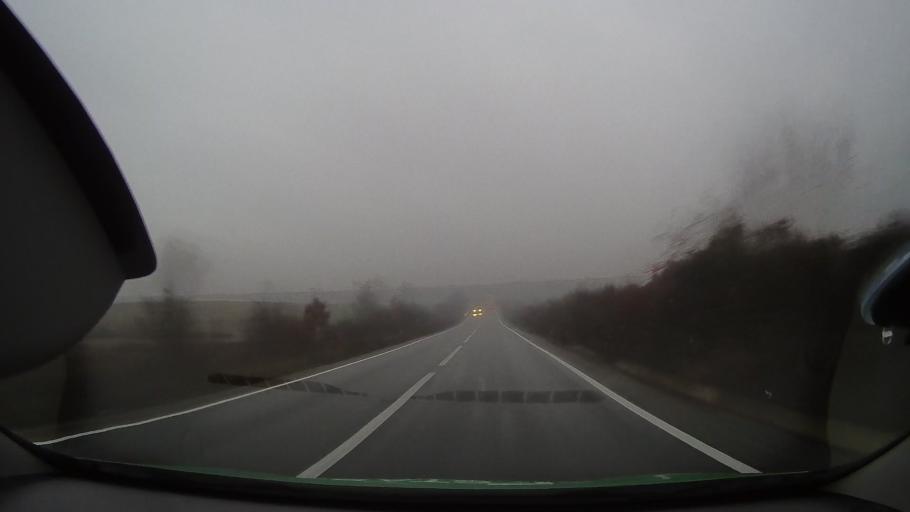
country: RO
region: Bihor
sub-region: Comuna Olcea
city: Olcea
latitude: 46.6820
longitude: 21.9665
